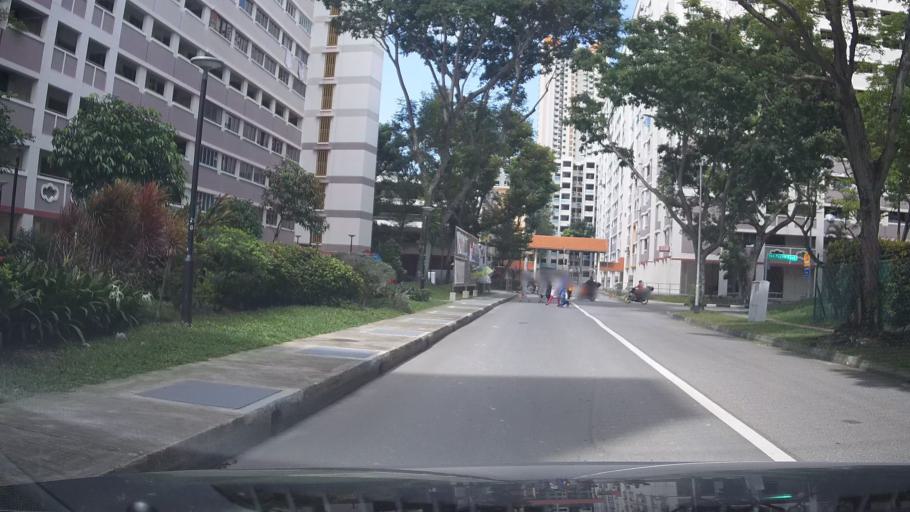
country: SG
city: Singapore
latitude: 1.3324
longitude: 103.8587
